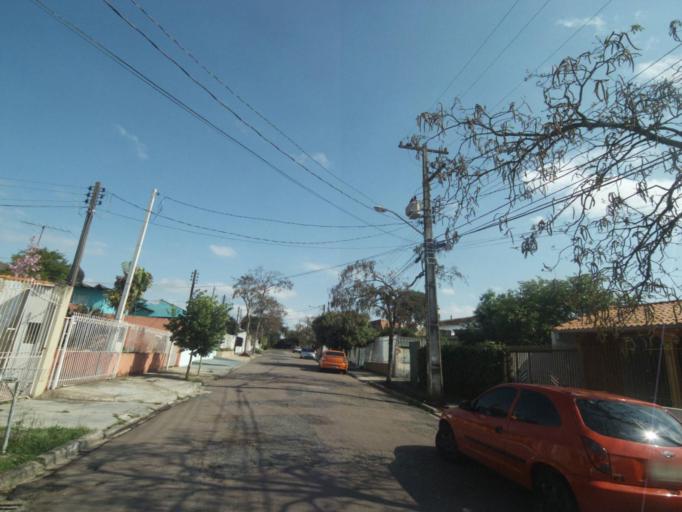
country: BR
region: Parana
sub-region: Pinhais
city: Pinhais
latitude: -25.4041
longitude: -49.2143
